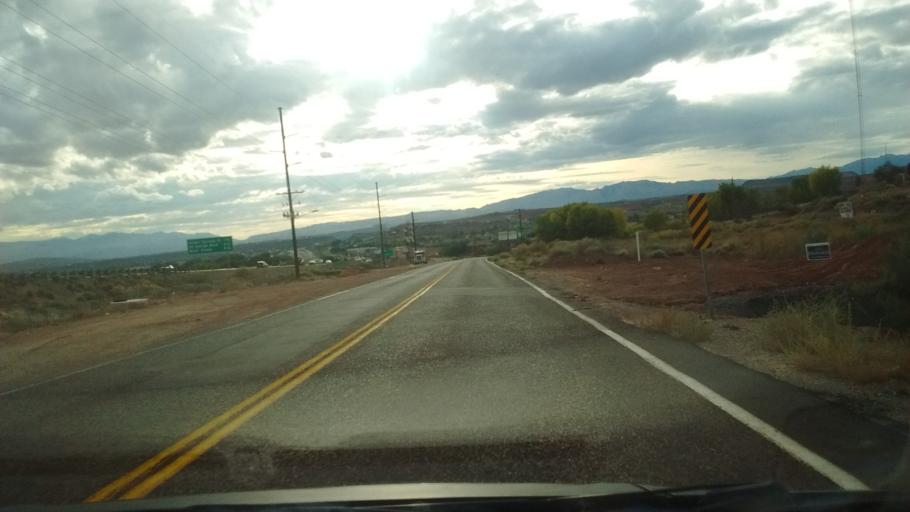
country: US
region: Utah
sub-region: Washington County
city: Washington
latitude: 37.1429
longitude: -113.5023
